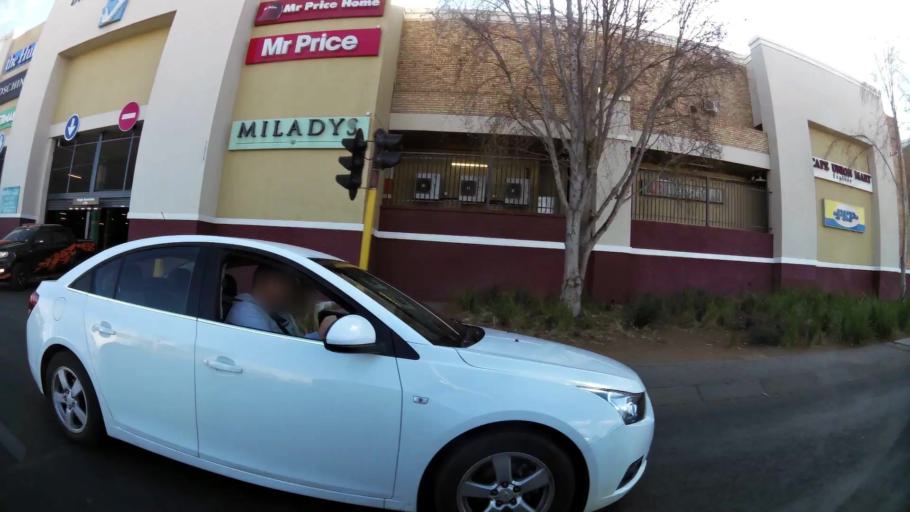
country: ZA
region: Northern Cape
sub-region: Frances Baard District Municipality
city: Kimberley
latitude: -28.7656
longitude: 24.7655
